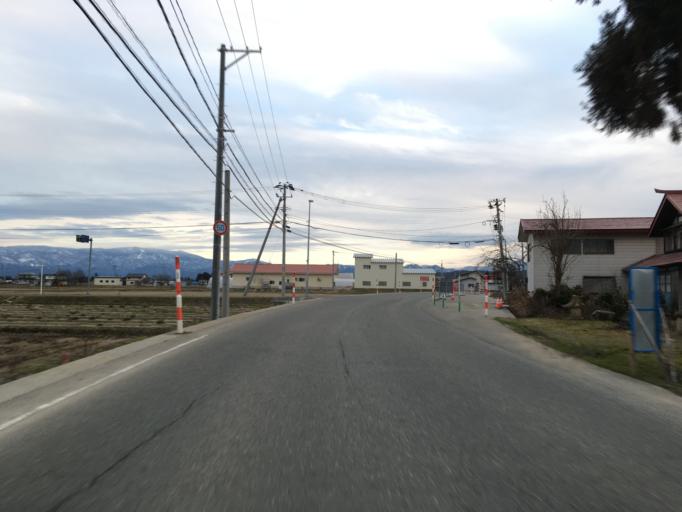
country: JP
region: Yamagata
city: Yonezawa
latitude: 37.9944
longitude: 140.0775
